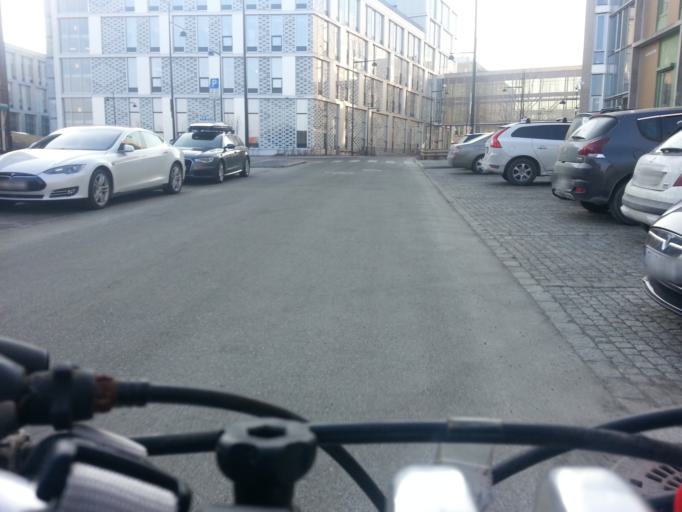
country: NO
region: Sor-Trondelag
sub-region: Trondheim
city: Trondheim
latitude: 63.4214
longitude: 10.3858
